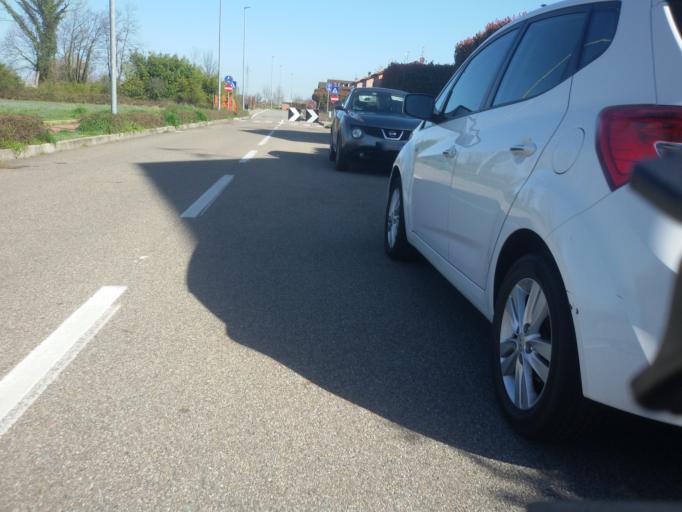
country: IT
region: Lombardy
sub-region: Citta metropolitana di Milano
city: Noviglio
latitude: 45.3607
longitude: 9.0467
